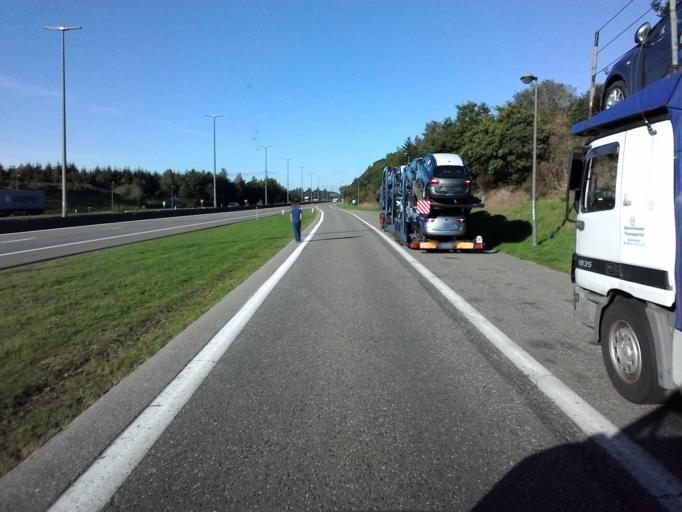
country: BE
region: Wallonia
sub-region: Province du Luxembourg
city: Bastogne
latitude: 50.0437
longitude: 5.7103
